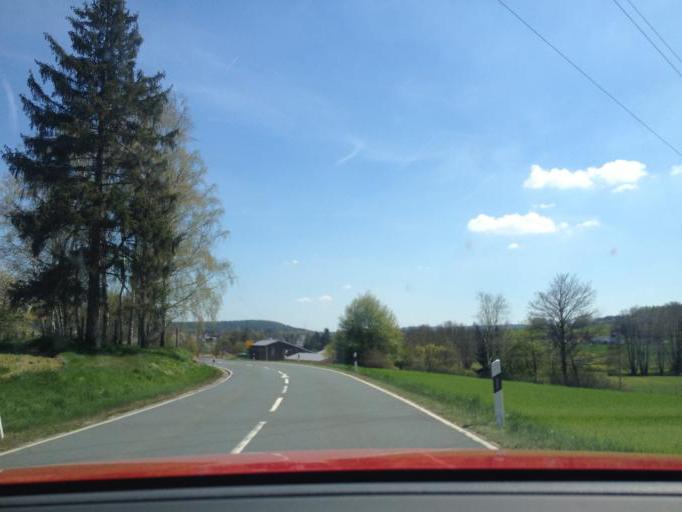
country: DE
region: Bavaria
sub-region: Upper Franconia
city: Marktleuthen
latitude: 50.1304
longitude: 11.9860
